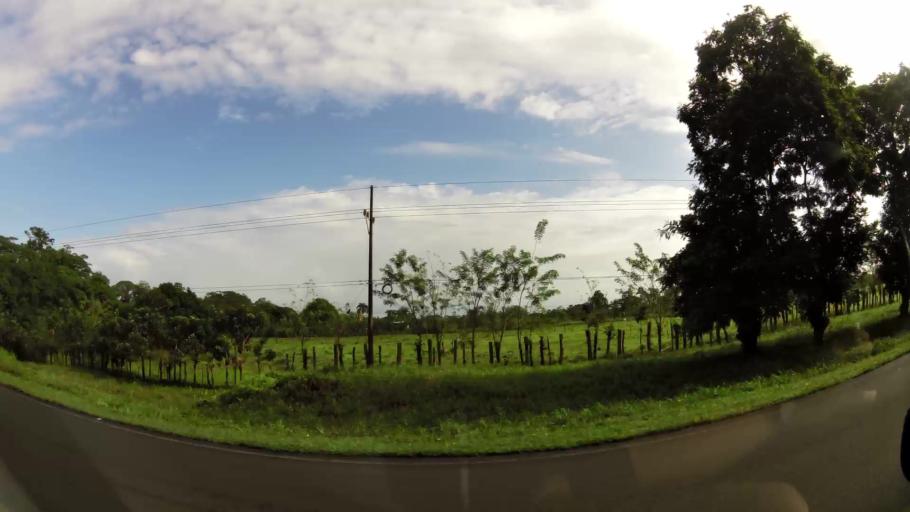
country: CR
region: Limon
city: Pocora
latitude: 10.1909
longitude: -83.6382
